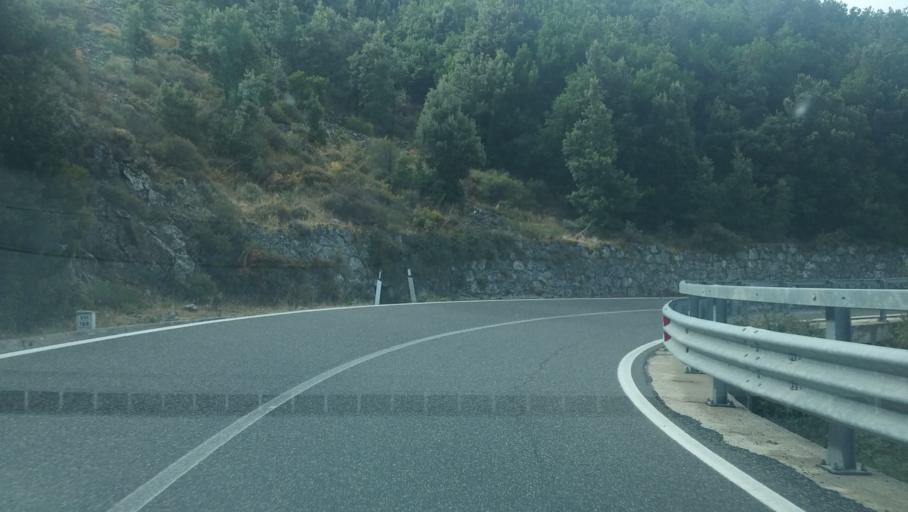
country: IT
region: Sardinia
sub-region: Provincia di Ogliastra
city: Urzulei
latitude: 40.1848
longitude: 9.5343
